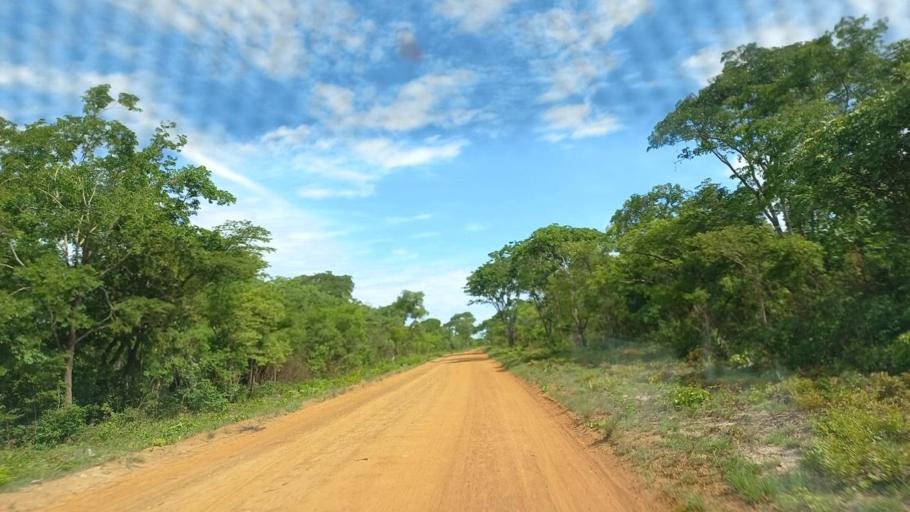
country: ZM
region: North-Western
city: Kabompo
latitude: -13.0781
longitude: 24.2191
